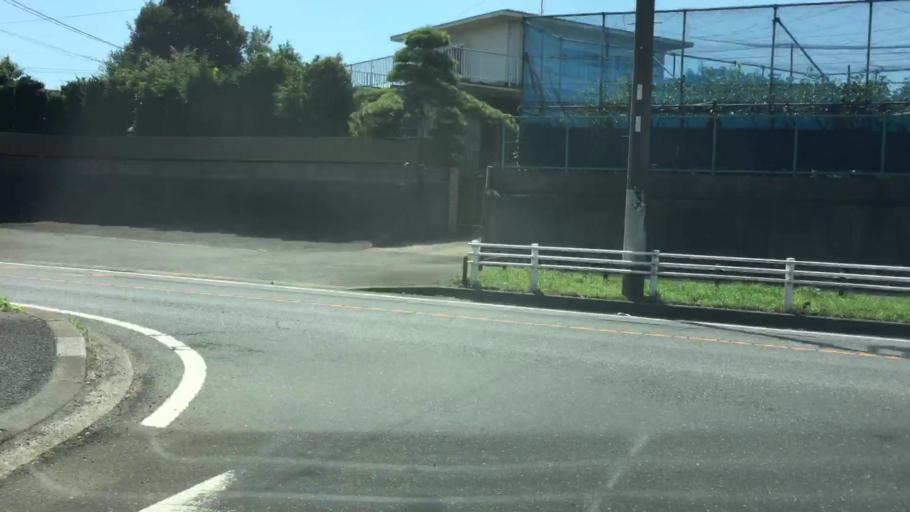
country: JP
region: Chiba
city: Matsudo
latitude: 35.7605
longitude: 139.9360
